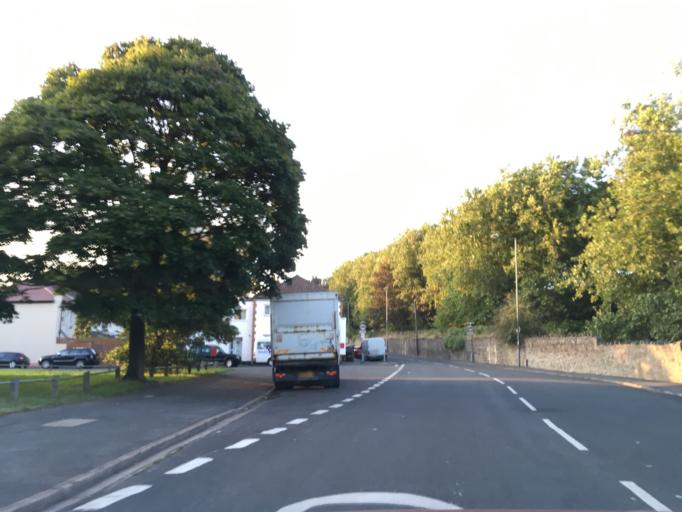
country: GB
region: England
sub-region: Bristol
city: Bristol
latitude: 51.4520
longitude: -2.5595
